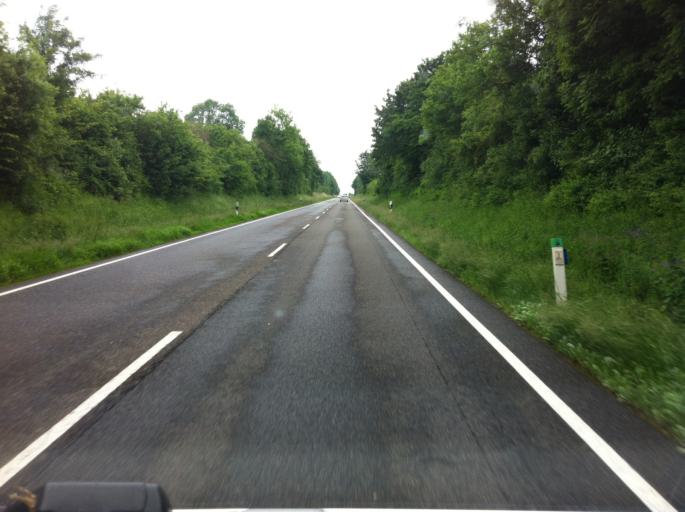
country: DE
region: North Rhine-Westphalia
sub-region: Regierungsbezirk Koln
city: Nettersheim
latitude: 50.5008
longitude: 6.6336
